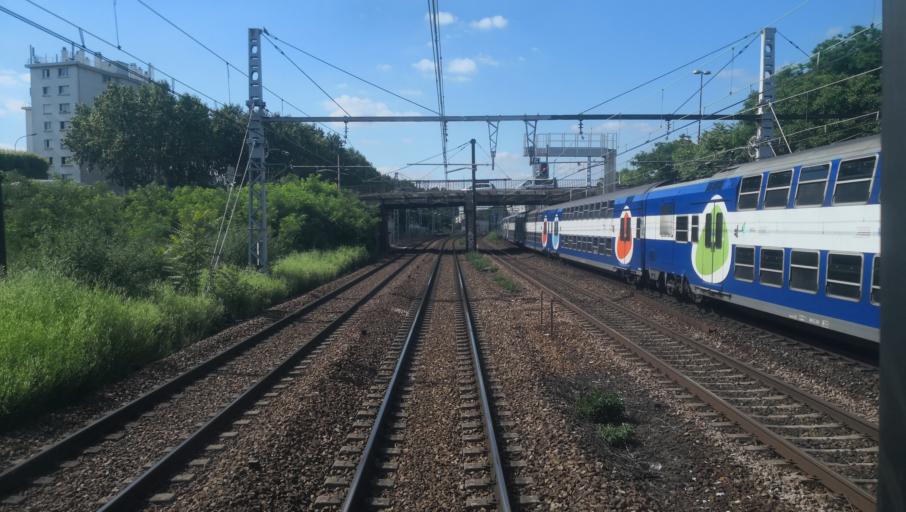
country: FR
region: Ile-de-France
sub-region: Departement du Val-de-Marne
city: Alfortville
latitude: 48.7992
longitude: 2.4280
